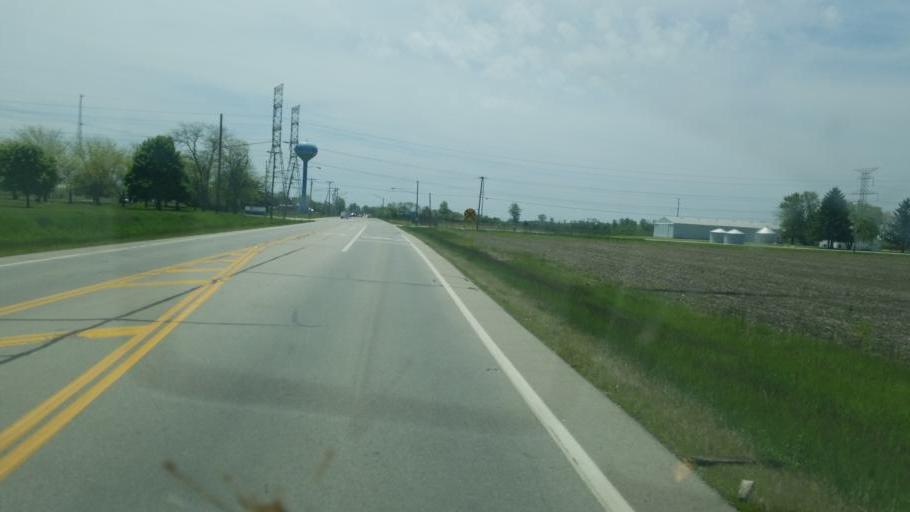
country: US
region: Ohio
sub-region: Ottawa County
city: Oak Harbor
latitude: 41.5972
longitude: -83.0969
